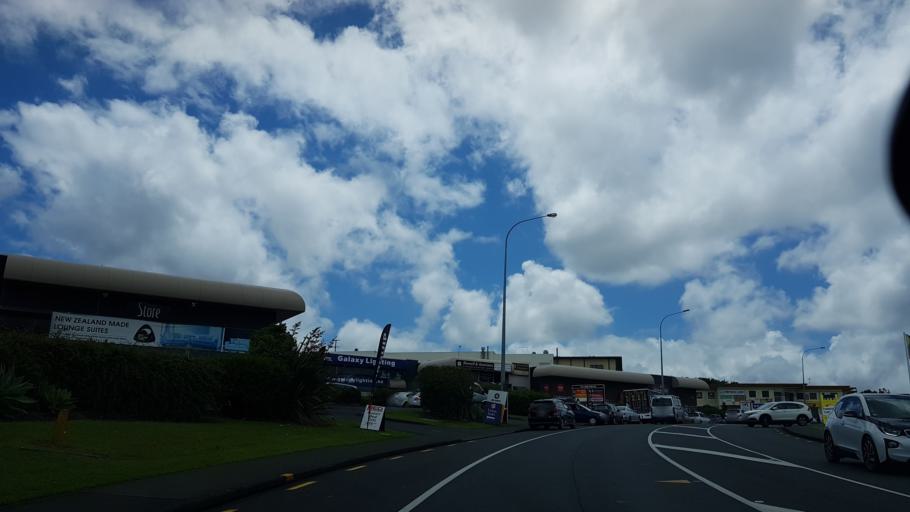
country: NZ
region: Auckland
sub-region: Auckland
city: North Shore
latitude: -36.7649
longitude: 174.7377
